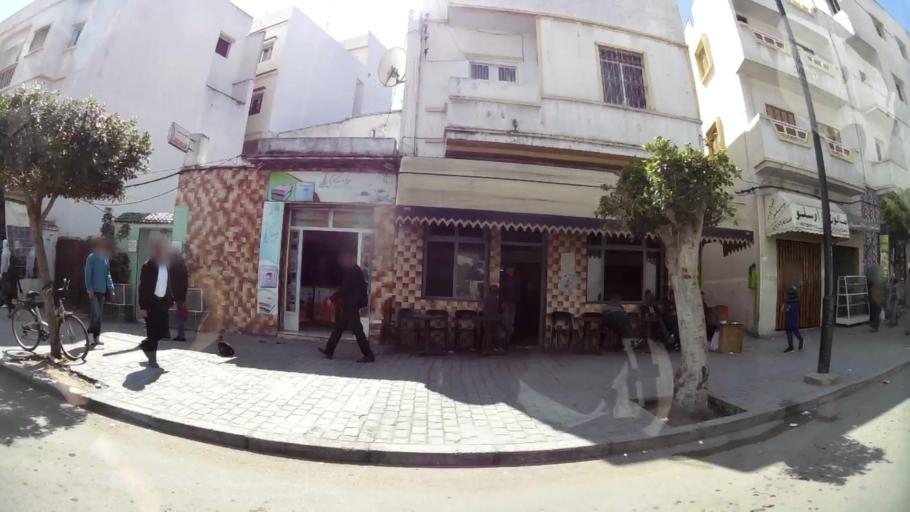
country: MA
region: Tanger-Tetouan
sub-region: Tanger-Assilah
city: Tangier
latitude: 35.7572
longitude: -5.8109
